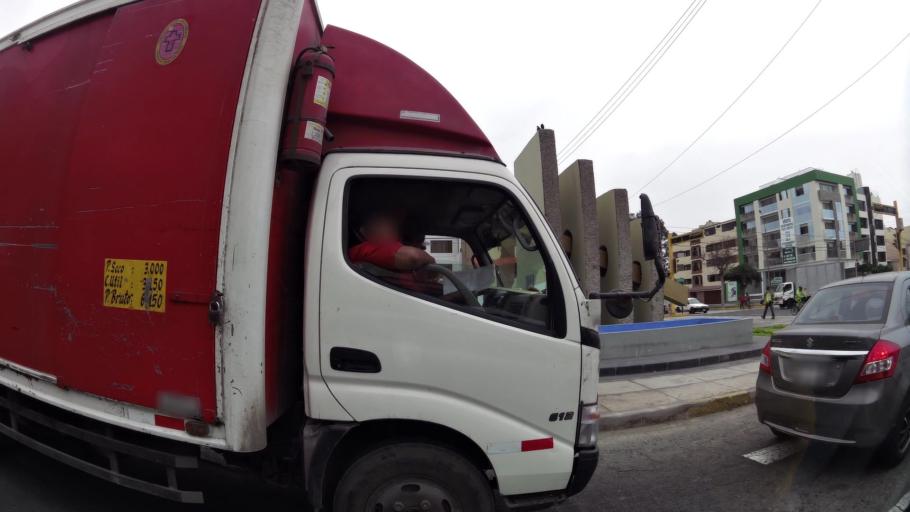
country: PE
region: Lima
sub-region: Lima
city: Surco
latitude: -12.1363
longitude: -77.0050
